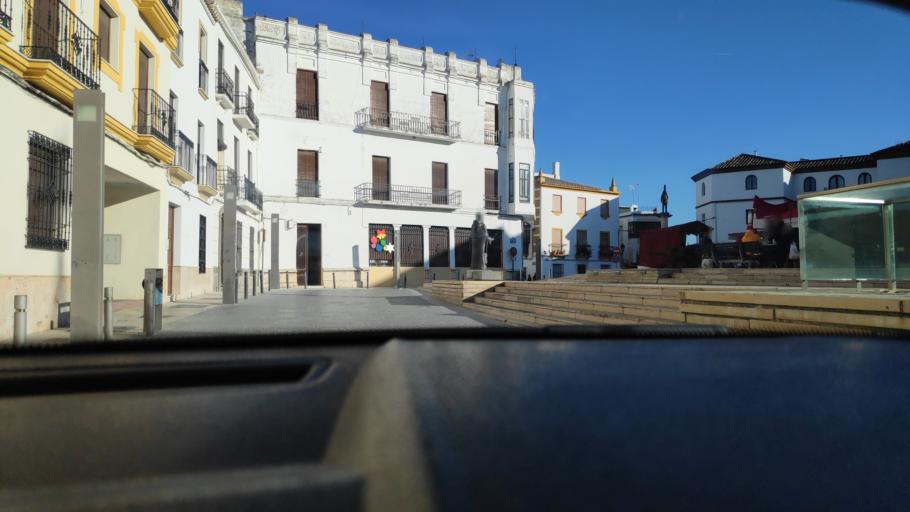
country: ES
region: Andalusia
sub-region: Province of Cordoba
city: Baena
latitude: 37.6146
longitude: -4.3258
